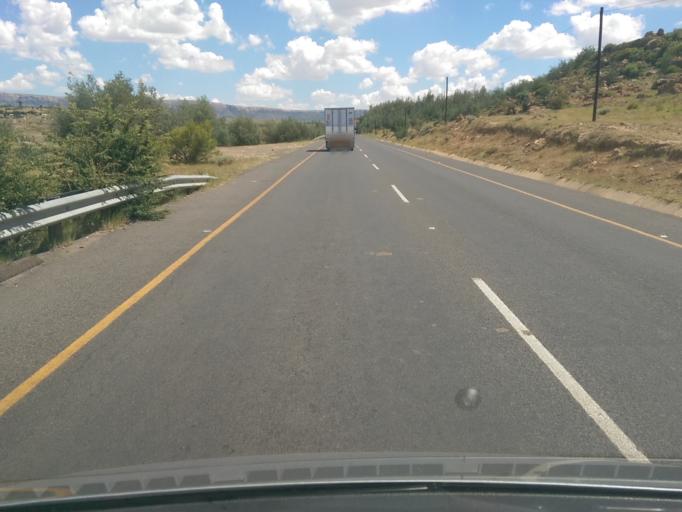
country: LS
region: Maseru
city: Maseru
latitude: -29.3974
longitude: 27.5358
